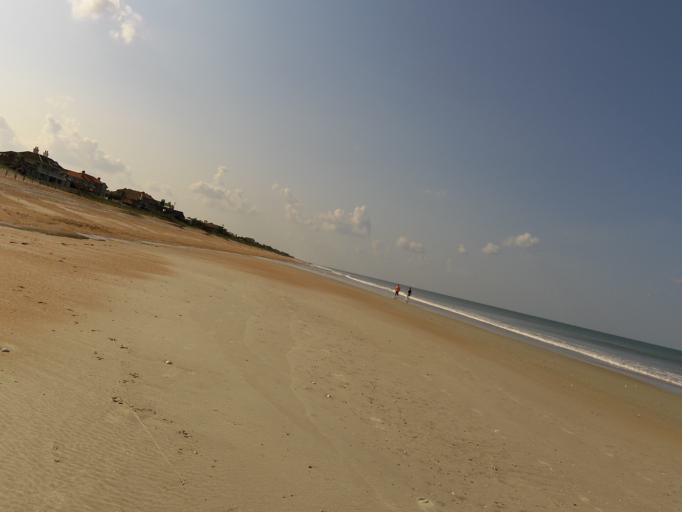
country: US
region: Florida
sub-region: Saint Johns County
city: Palm Valley
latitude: 30.1457
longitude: -81.3512
